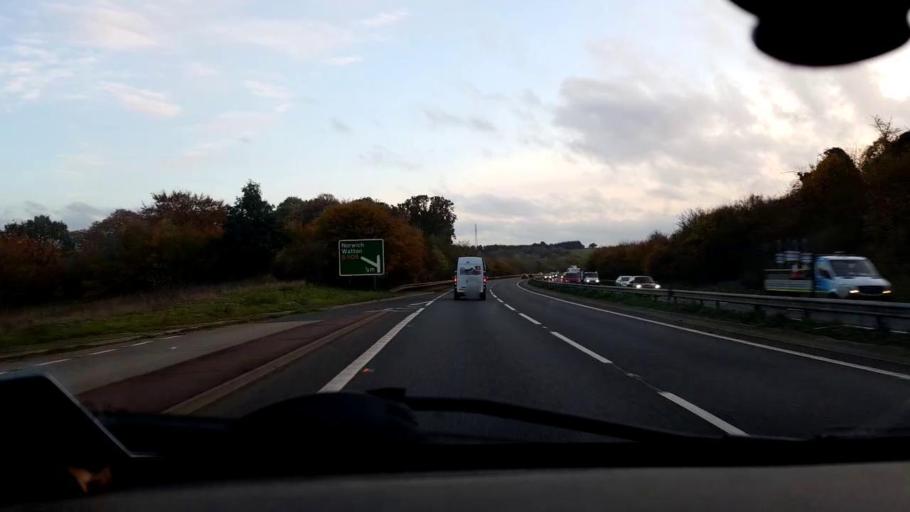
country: GB
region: England
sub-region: Norfolk
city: Bowthorpe
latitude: 52.6365
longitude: 1.1959
